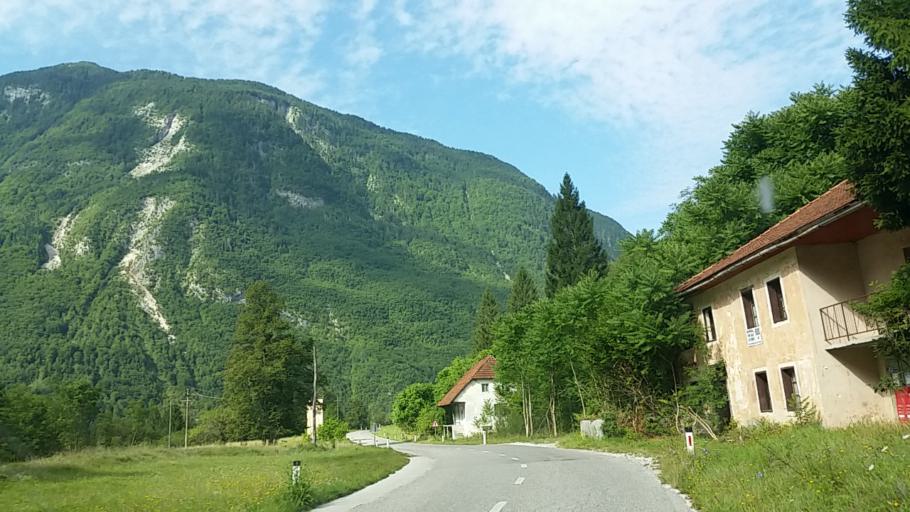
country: SI
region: Bovec
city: Bovec
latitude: 46.3379
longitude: 13.6452
